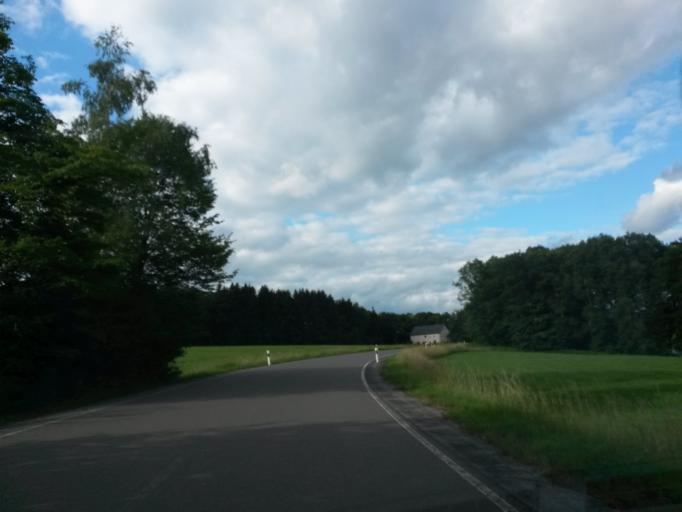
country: DE
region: North Rhine-Westphalia
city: Meinerzhagen
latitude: 51.0922
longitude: 7.6917
